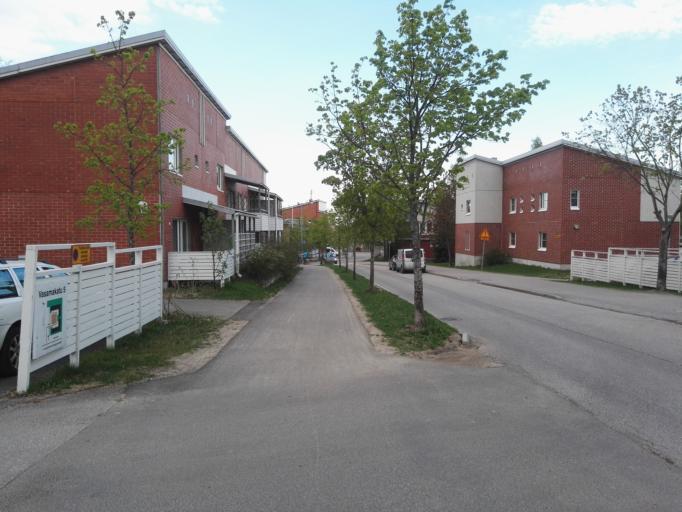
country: FI
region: Paijanne Tavastia
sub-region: Lahti
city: Lahti
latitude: 60.9748
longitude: 25.6470
